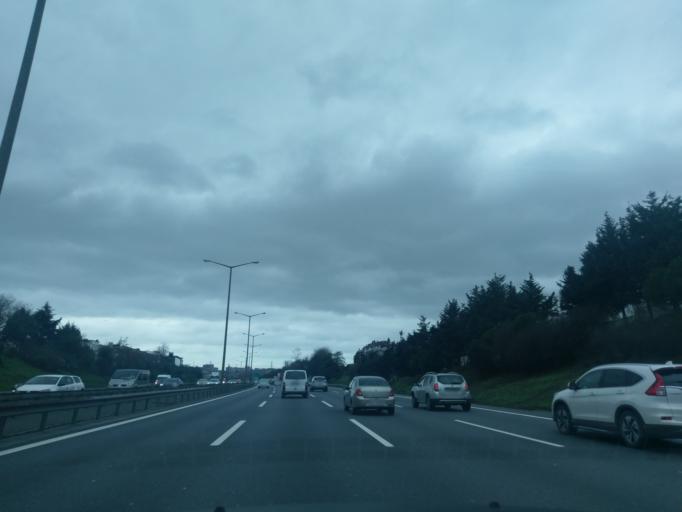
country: TR
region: Istanbul
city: Sultangazi
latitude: 41.0914
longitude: 28.8955
